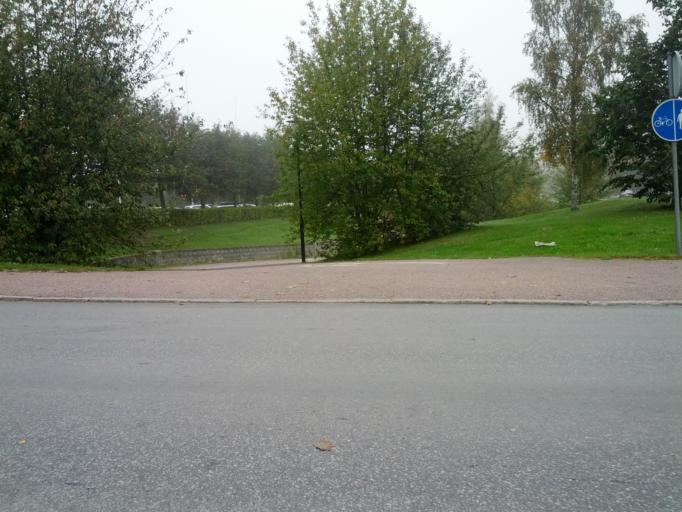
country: SE
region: Uppsala
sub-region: Uppsala Kommun
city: Uppsala
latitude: 59.8415
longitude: 17.6387
